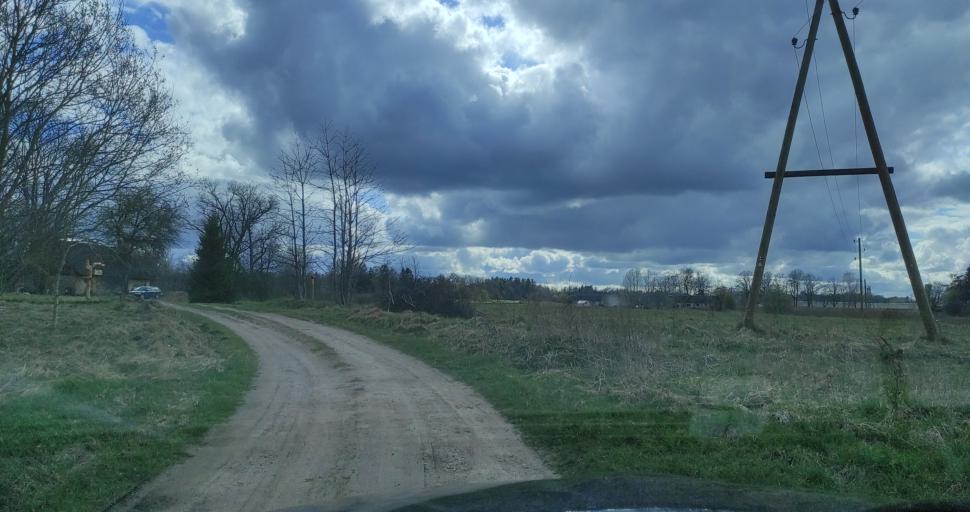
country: LV
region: Aizpute
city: Aizpute
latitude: 56.7127
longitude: 21.5919
